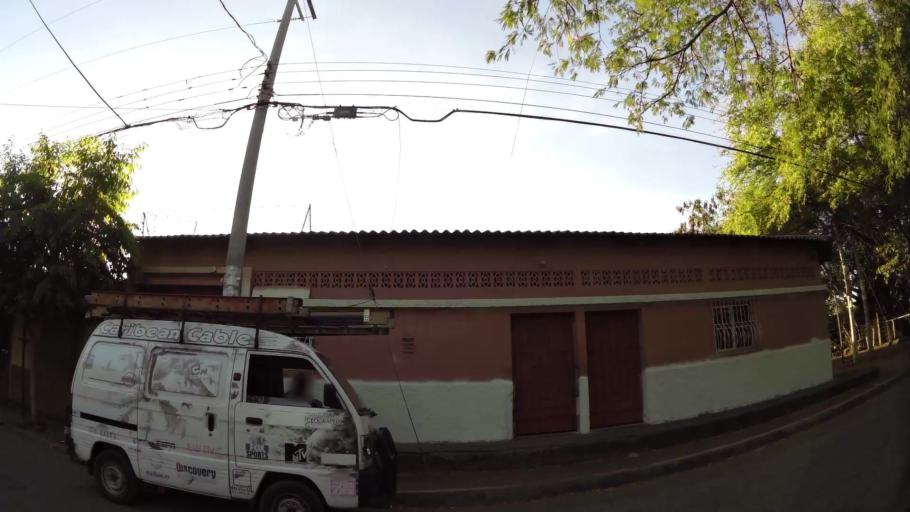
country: SV
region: San Miguel
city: San Miguel
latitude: 13.4663
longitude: -88.1689
